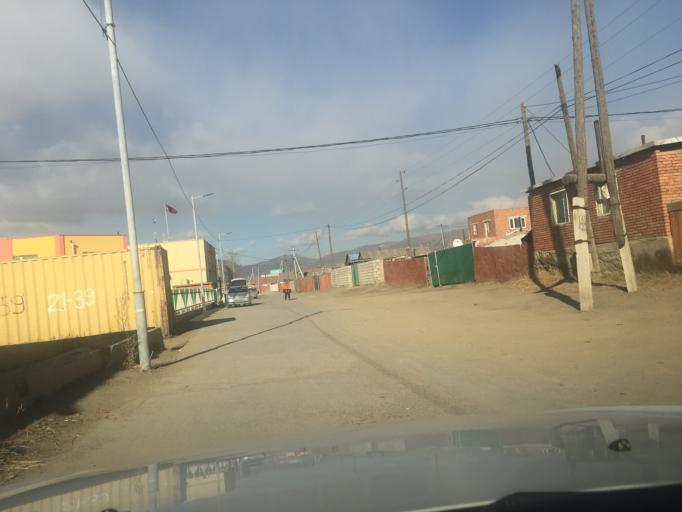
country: MN
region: Ulaanbaatar
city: Ulaanbaatar
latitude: 47.9451
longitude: 106.8253
